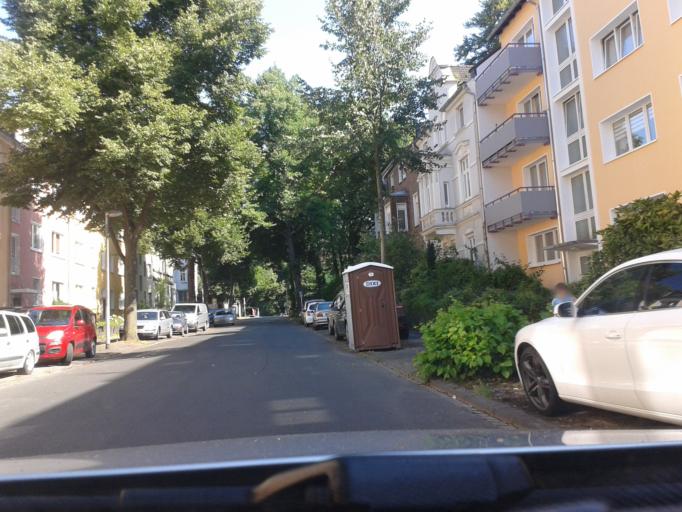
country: DE
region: North Rhine-Westphalia
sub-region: Regierungsbezirk Dusseldorf
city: Muelheim (Ruhr)
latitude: 51.4332
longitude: 6.8930
